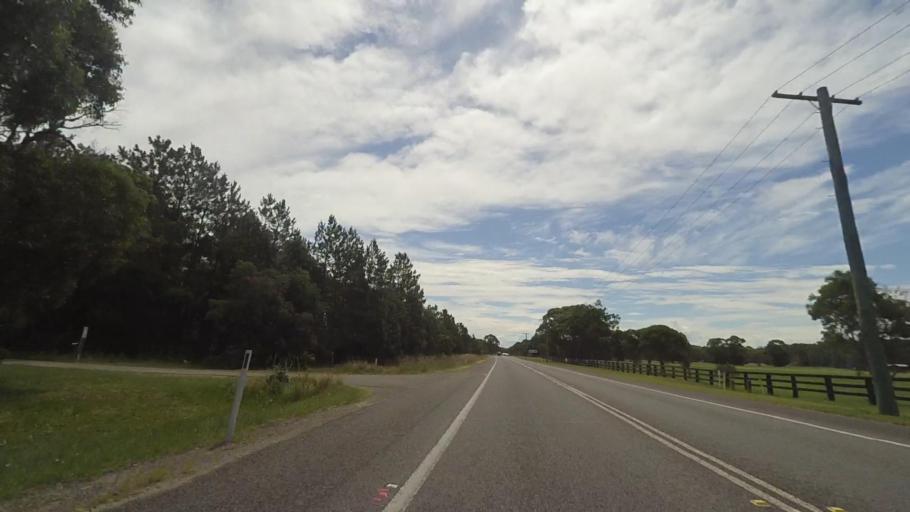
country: AU
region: New South Wales
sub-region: Port Stephens Shire
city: Medowie
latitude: -32.7859
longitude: 151.8974
